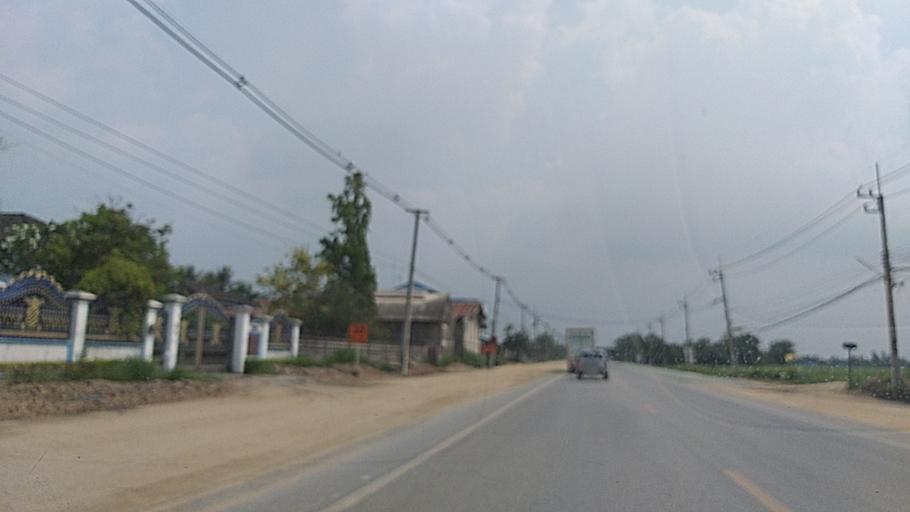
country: TH
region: Chon Buri
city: Phanat Nikhom
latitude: 13.3725
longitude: 101.1951
